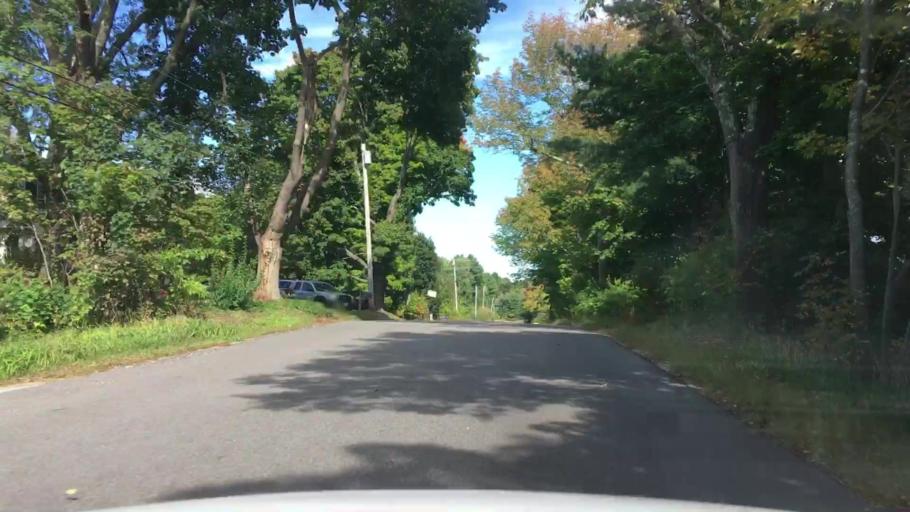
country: US
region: Maine
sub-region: Cumberland County
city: Westbrook
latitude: 43.6704
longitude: -70.3937
